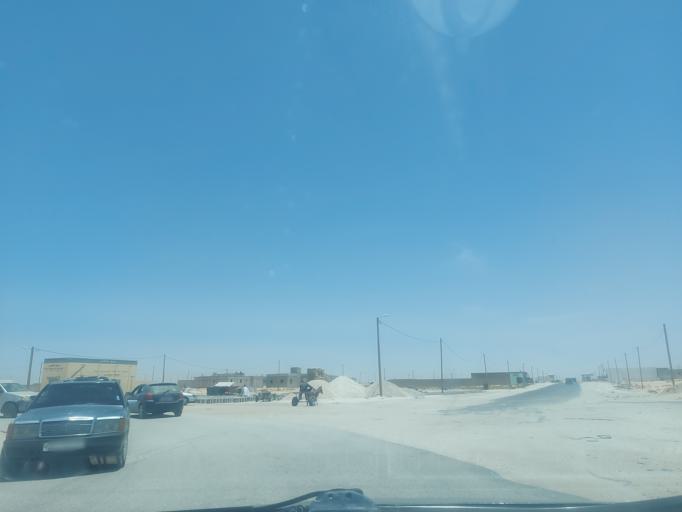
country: MR
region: Nouakchott
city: Nouakchott
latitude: 18.0859
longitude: -15.9517
